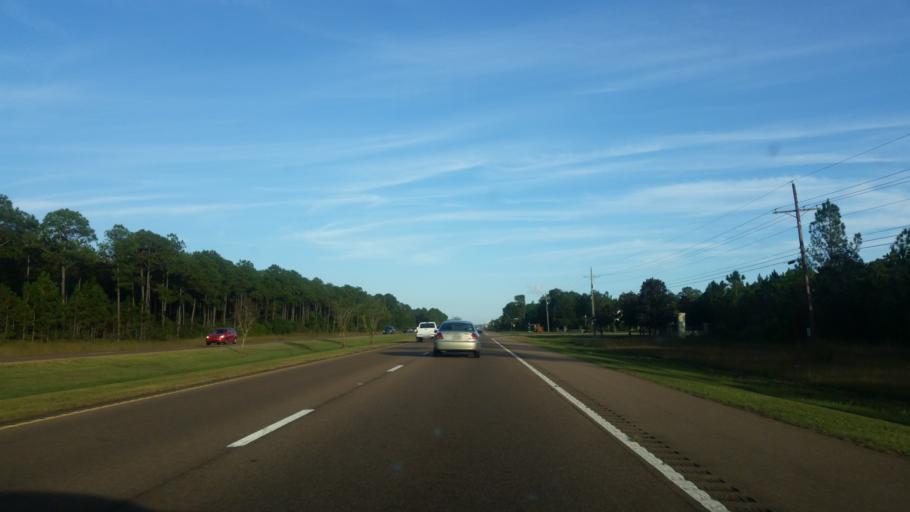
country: US
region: Mississippi
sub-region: Jackson County
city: Gautier
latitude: 30.3961
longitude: -88.6798
